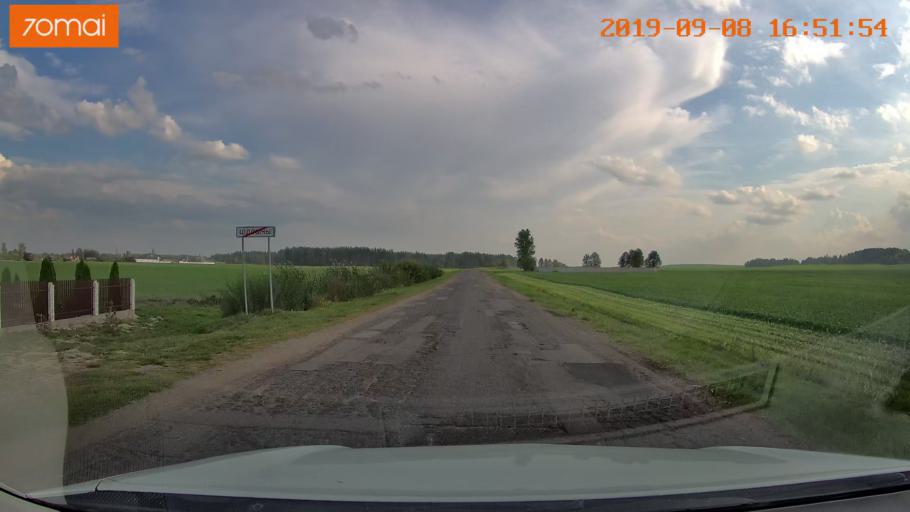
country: BY
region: Grodnenskaya
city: Hrodna
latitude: 53.7809
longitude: 23.8985
